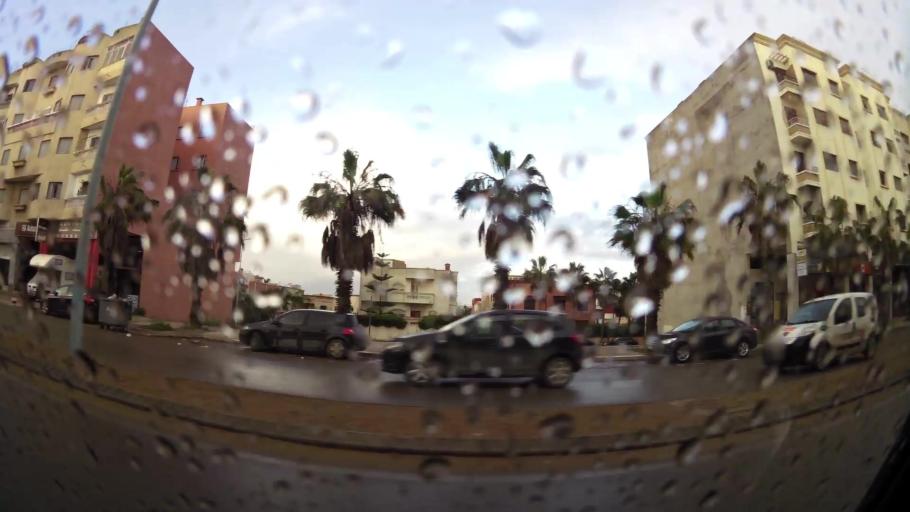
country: MA
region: Doukkala-Abda
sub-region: El-Jadida
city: El Jadida
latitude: 33.2270
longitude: -8.4934
